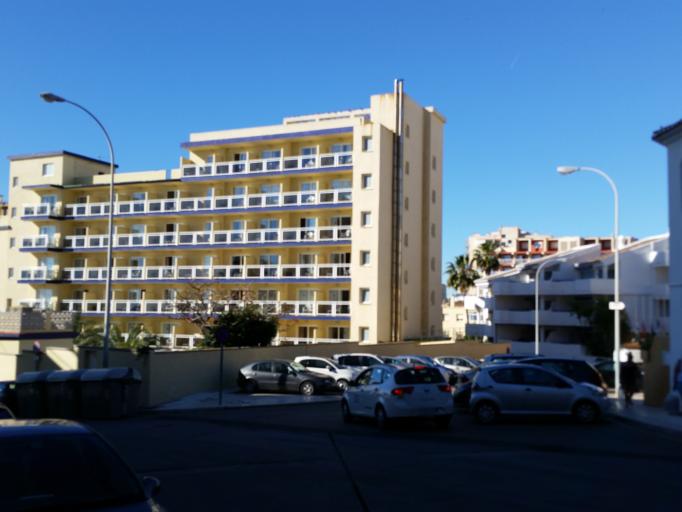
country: ES
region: Andalusia
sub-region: Provincia de Malaga
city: Benalmadena
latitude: 36.5900
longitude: -4.5294
